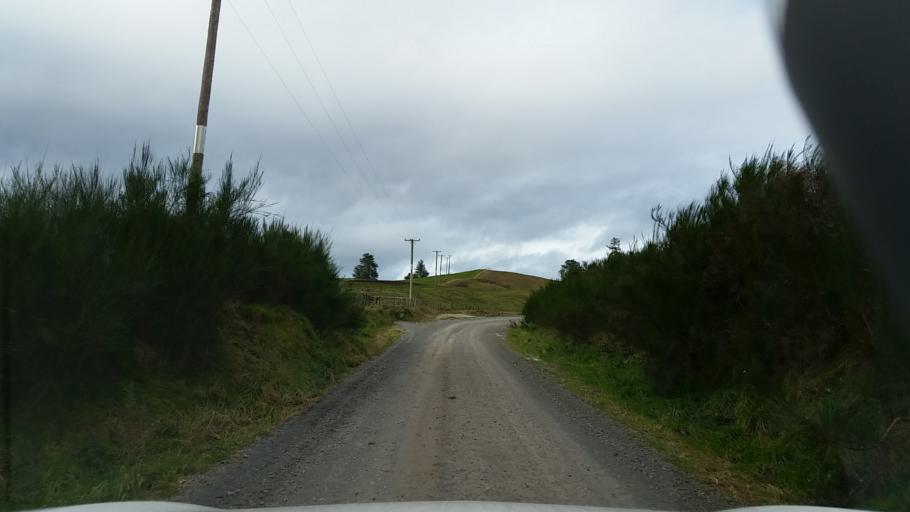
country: NZ
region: Bay of Plenty
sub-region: Whakatane District
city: Murupara
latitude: -38.3377
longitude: 176.5386
